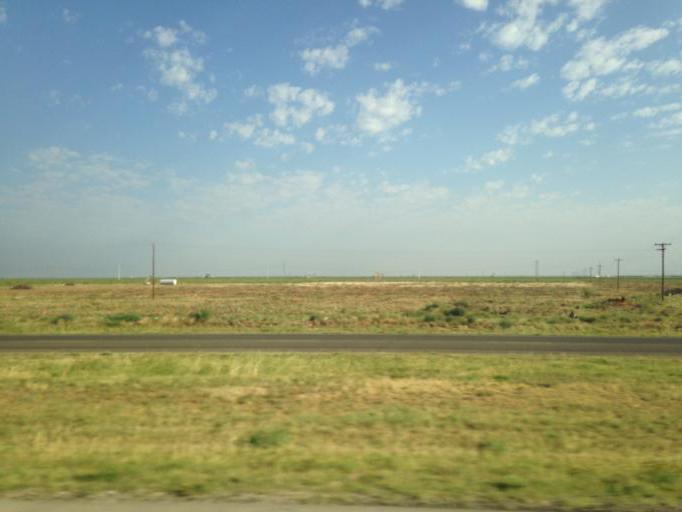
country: US
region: Texas
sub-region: Midland County
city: Midland
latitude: 32.0636
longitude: -101.9431
